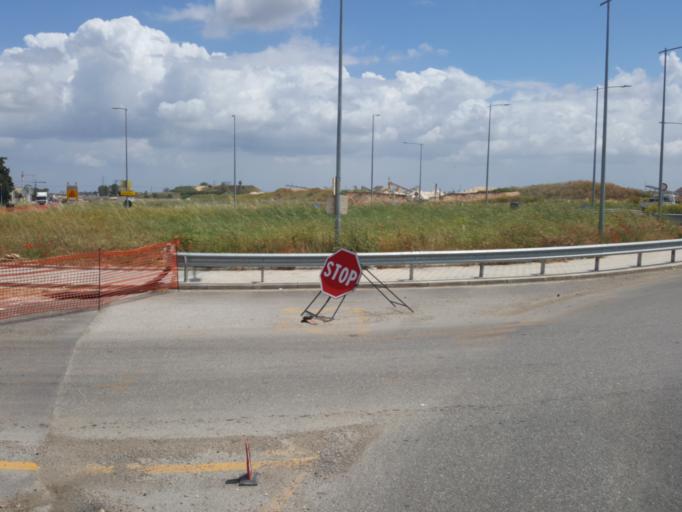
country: IT
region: Apulia
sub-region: Provincia di Bari
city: Palo del Colle
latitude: 41.0668
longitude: 16.7267
